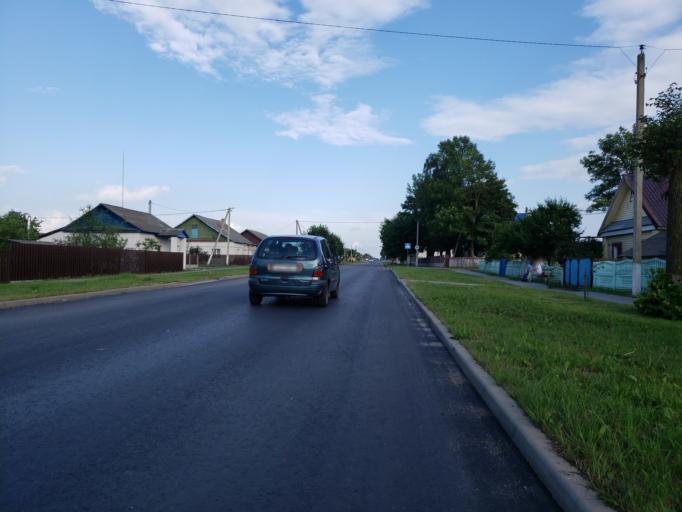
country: BY
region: Minsk
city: Chervyen'
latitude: 53.7041
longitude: 28.4382
